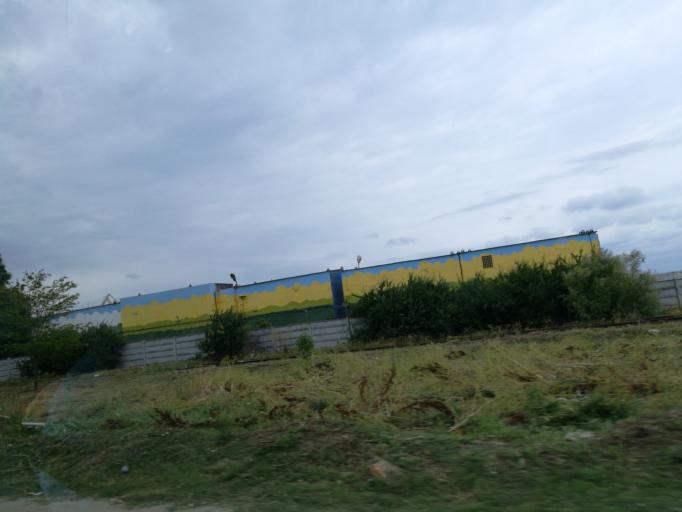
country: RO
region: Constanta
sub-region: Municipiul Mangalia
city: Mangalia
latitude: 43.7932
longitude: 28.5758
